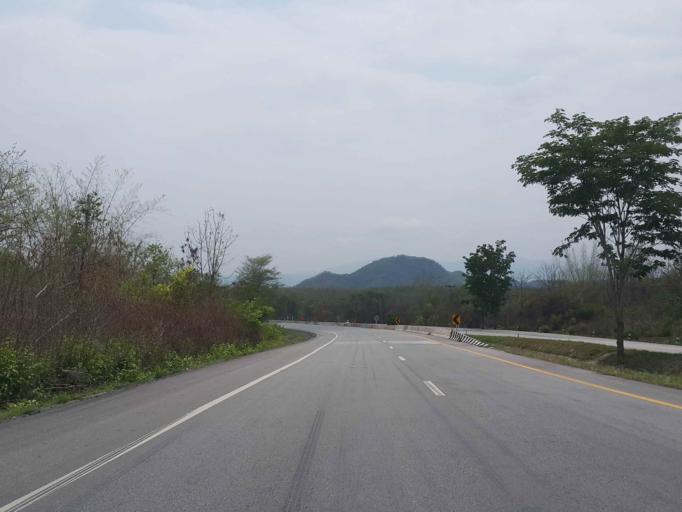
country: TH
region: Lampang
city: Sop Prap
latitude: 17.9719
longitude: 99.3545
